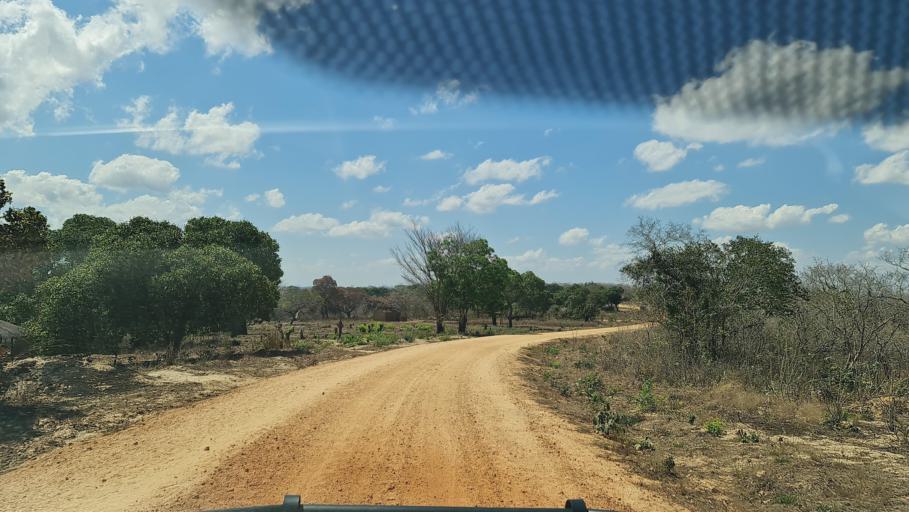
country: MZ
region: Nampula
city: Nacala
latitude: -14.1762
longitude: 40.2172
